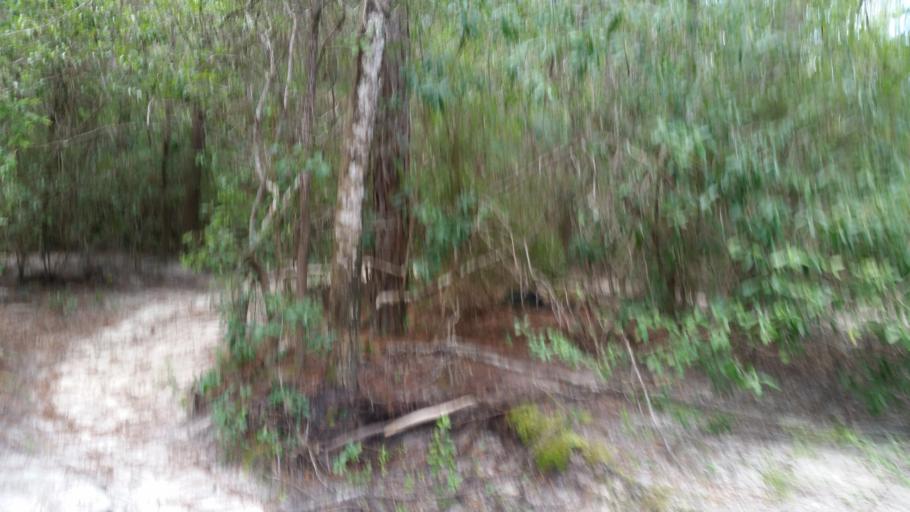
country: US
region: Florida
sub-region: Santa Rosa County
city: East Milton
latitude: 30.7068
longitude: -86.8773
